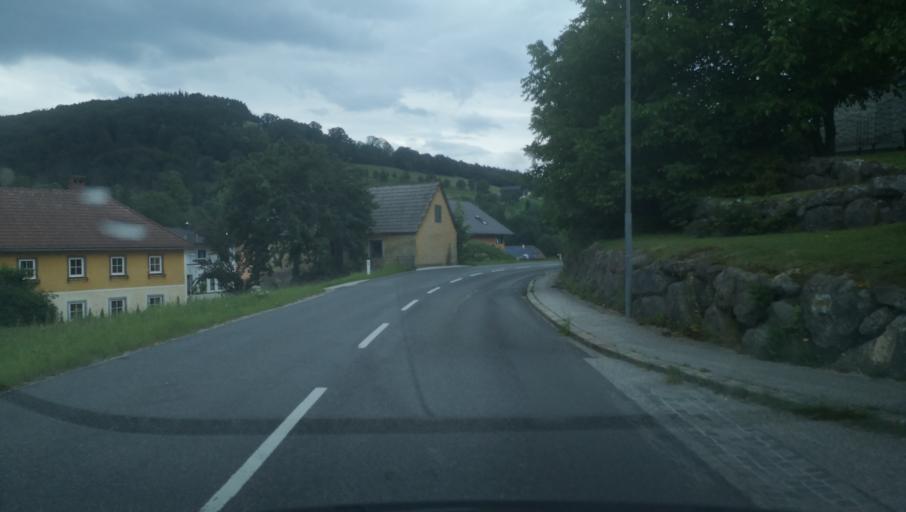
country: AT
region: Lower Austria
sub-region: Politischer Bezirk Scheibbs
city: Randegg
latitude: 48.0123
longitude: 14.9516
